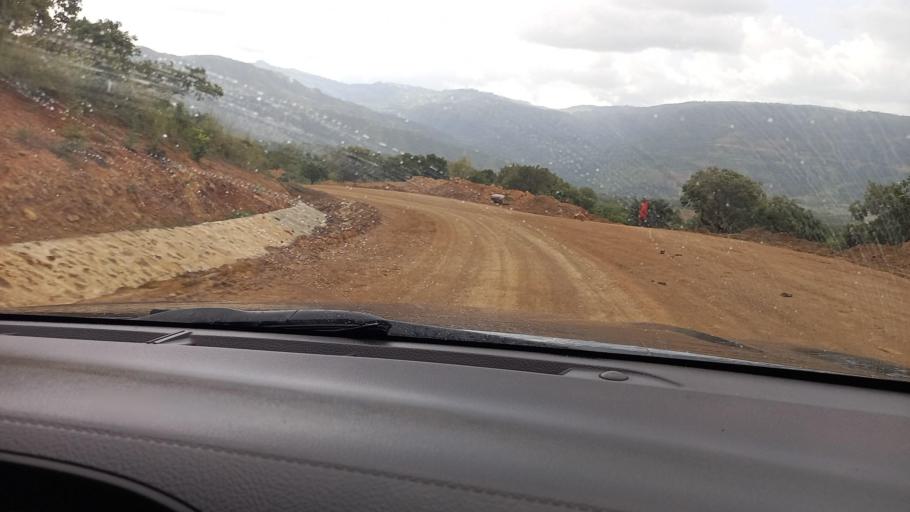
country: ET
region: Southern Nations, Nationalities, and People's Region
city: Mizan Teferi
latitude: 6.1821
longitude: 35.6992
